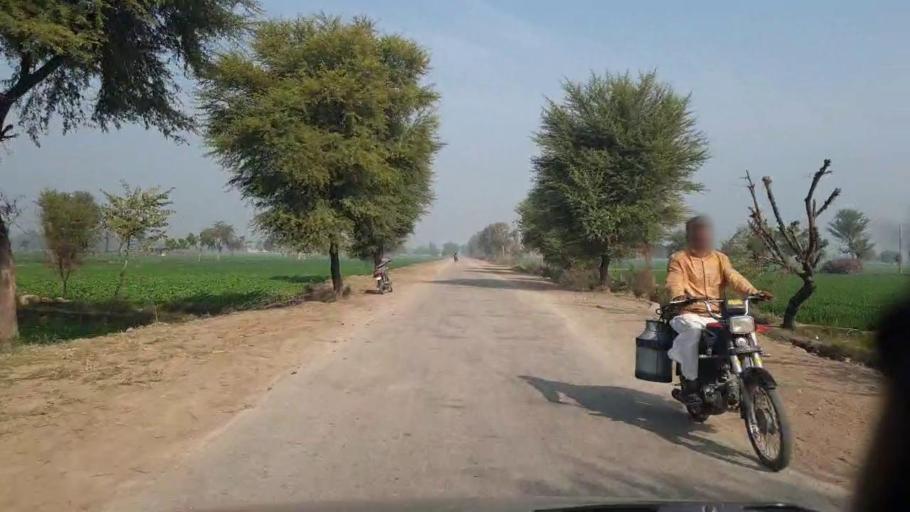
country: PK
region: Sindh
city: Shahdadpur
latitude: 26.0176
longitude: 68.5463
